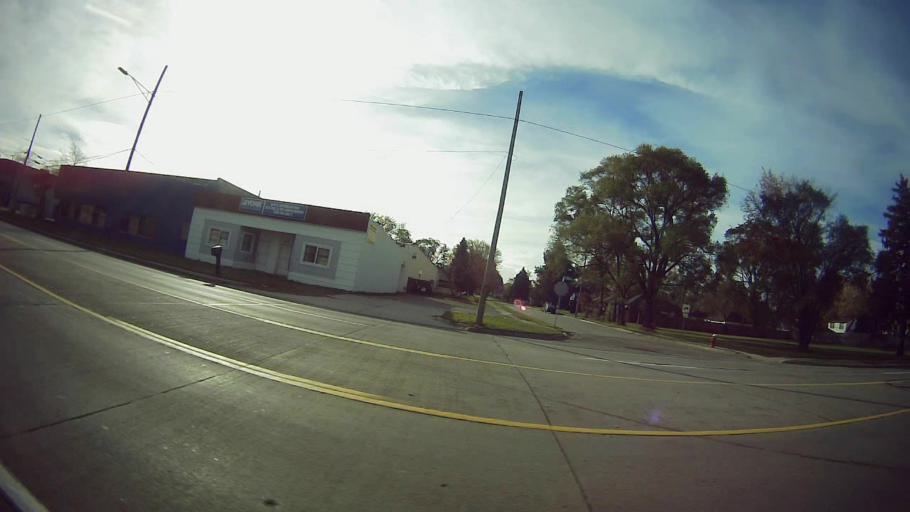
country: US
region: Michigan
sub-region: Macomb County
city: Warren
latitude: 42.4625
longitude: -83.0499
